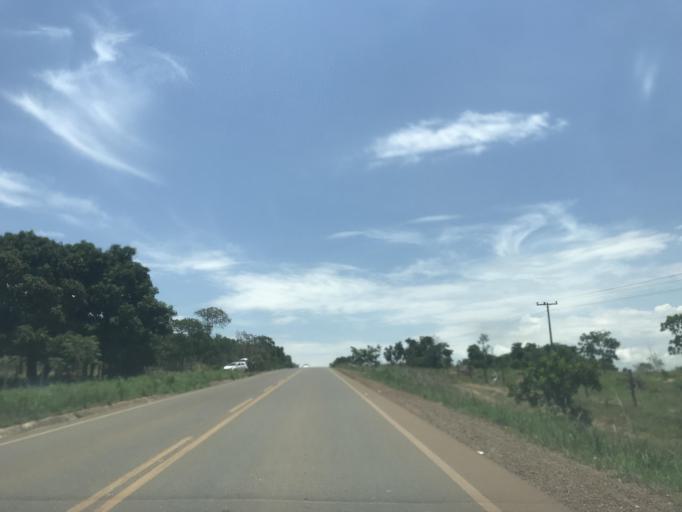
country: BR
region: Goias
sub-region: Vianopolis
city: Vianopolis
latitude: -16.6141
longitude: -48.3517
